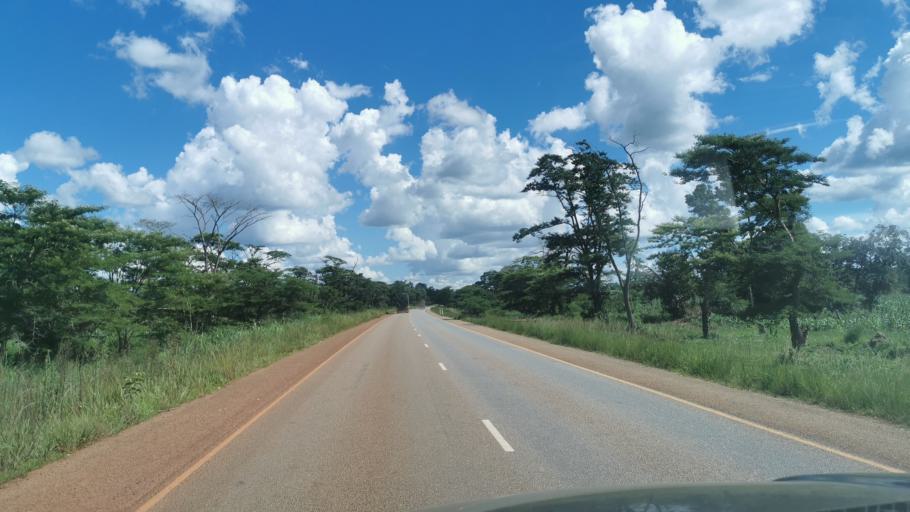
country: TZ
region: Geita
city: Uyovu
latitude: -3.0481
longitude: 31.2516
